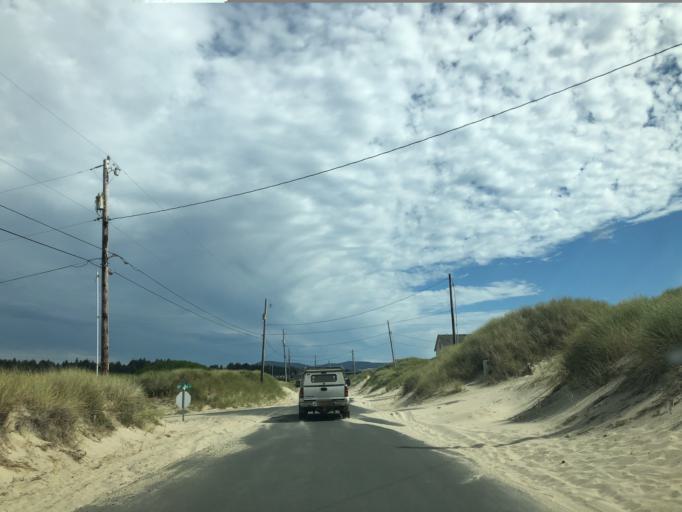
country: US
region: Oregon
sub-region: Lincoln County
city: Waldport
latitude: 44.4285
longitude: -124.0822
